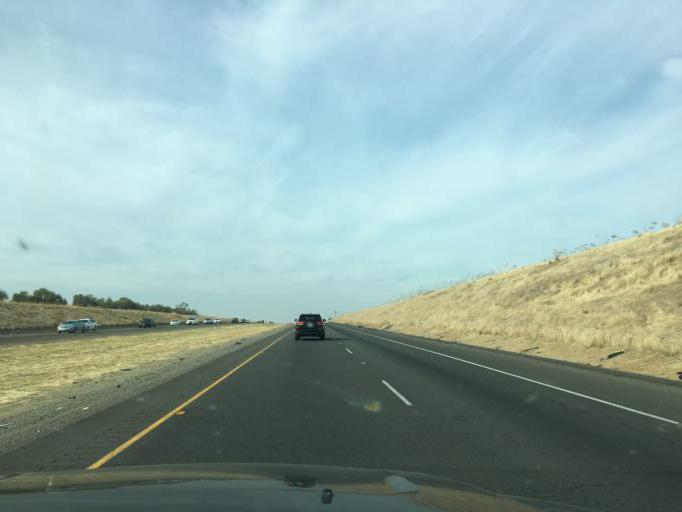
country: US
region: California
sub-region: Merced County
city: Los Banos
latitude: 37.0080
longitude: -120.9225
